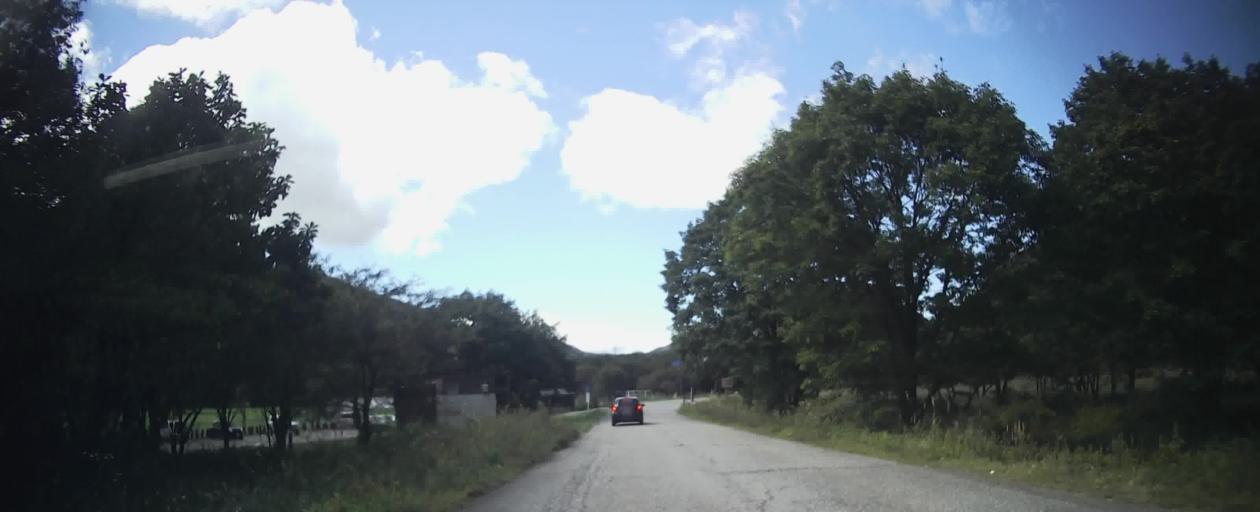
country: JP
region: Gunma
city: Shibukawa
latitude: 36.4698
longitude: 138.8832
